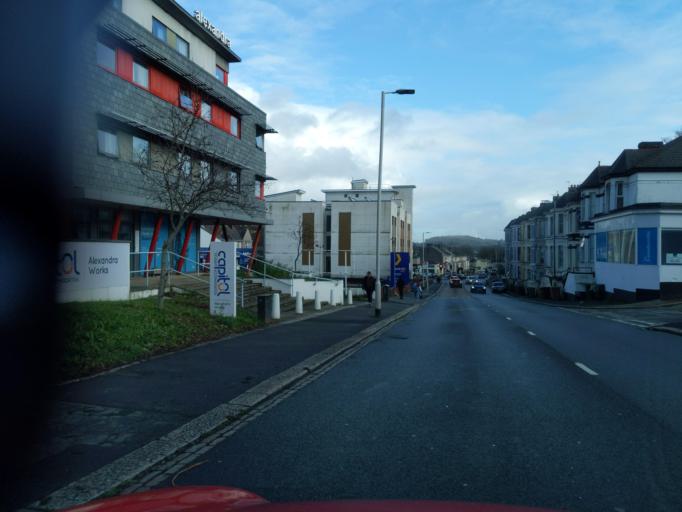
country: GB
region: England
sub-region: Plymouth
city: Plymouth
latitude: 50.3819
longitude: -4.1264
